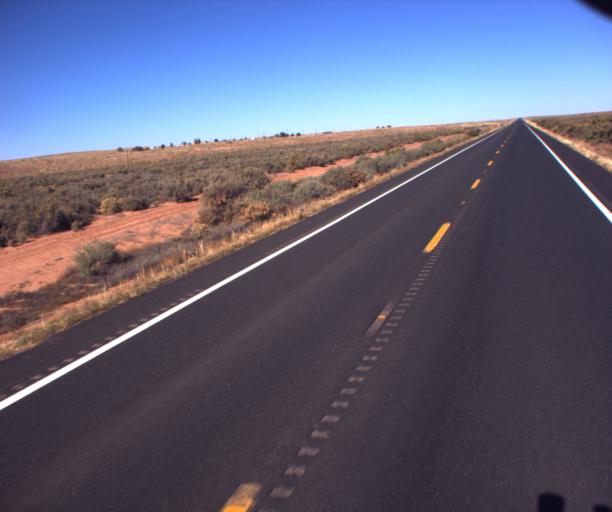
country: US
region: Arizona
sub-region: Coconino County
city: Kaibito
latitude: 36.3402
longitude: -110.9178
